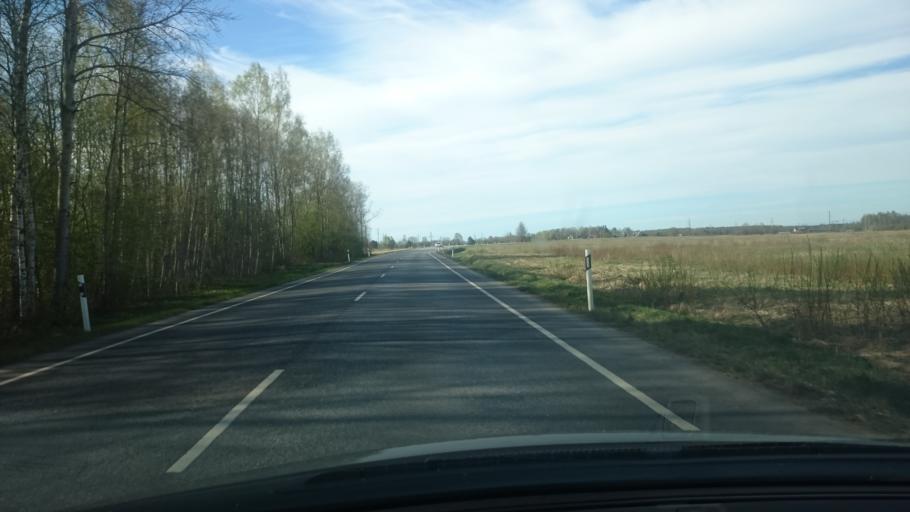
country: EE
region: Ida-Virumaa
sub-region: Johvi vald
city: Johvi
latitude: 59.2584
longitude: 27.5156
